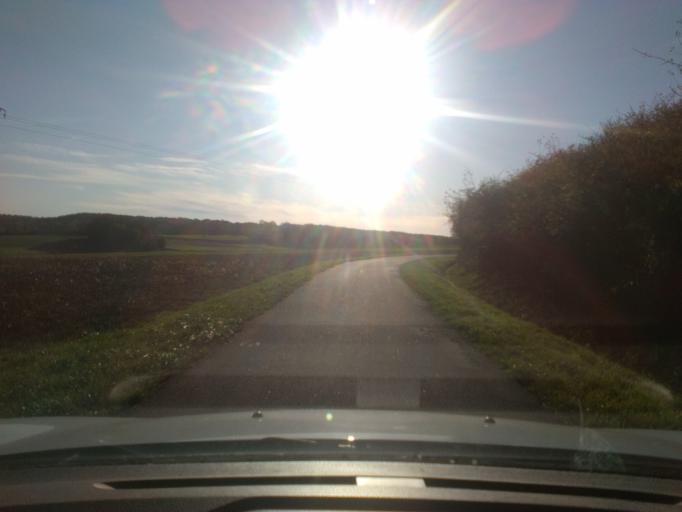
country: FR
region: Lorraine
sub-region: Departement des Vosges
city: Rambervillers
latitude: 48.2887
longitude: 6.6281
